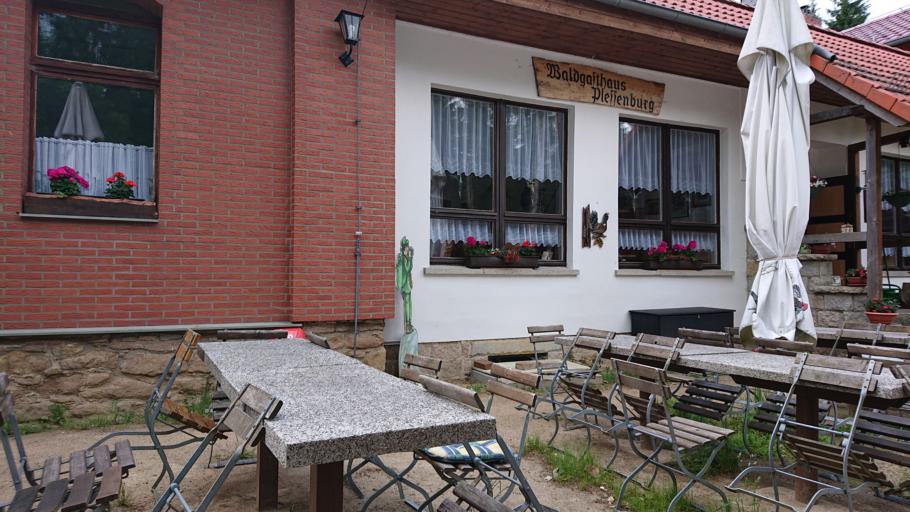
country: DE
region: Saxony-Anhalt
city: Ilsenburg
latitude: 51.8321
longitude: 10.6681
